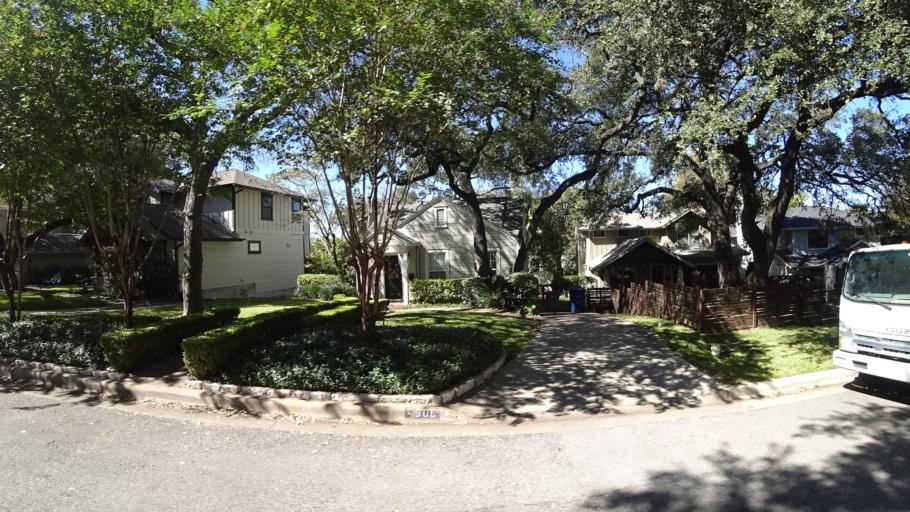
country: US
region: Texas
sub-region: Travis County
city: Austin
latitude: 30.3211
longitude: -97.7426
